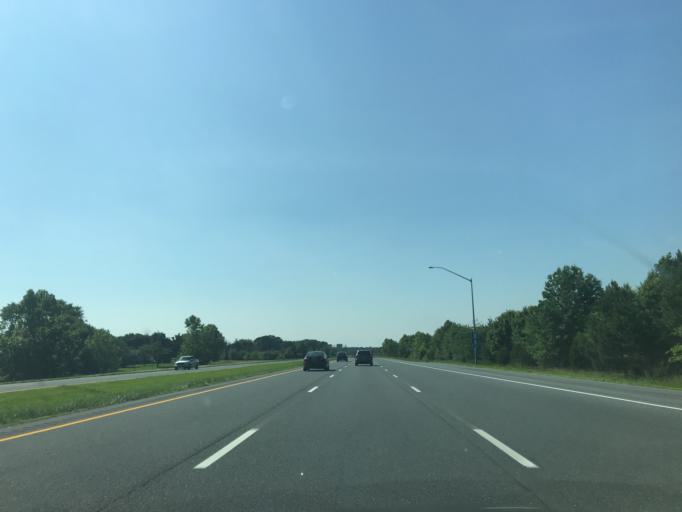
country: US
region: Maryland
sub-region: Wicomico County
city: Hebron
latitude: 38.4050
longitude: -75.6365
